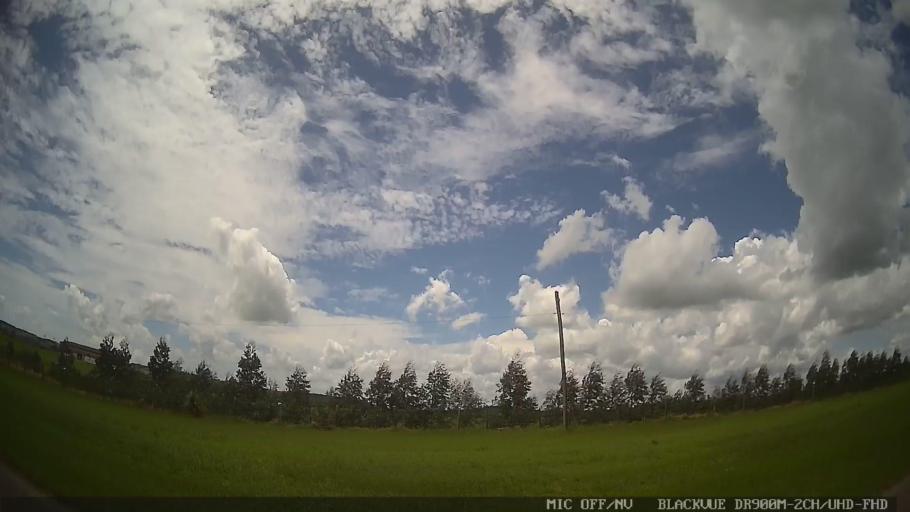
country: BR
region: Sao Paulo
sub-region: Conchas
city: Conchas
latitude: -23.0454
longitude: -47.9331
